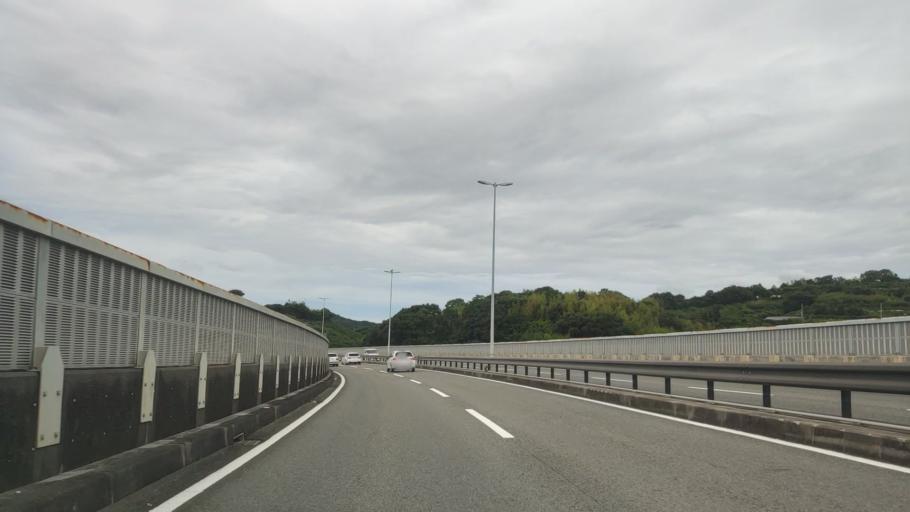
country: JP
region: Wakayama
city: Tanabe
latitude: 33.7433
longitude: 135.3859
